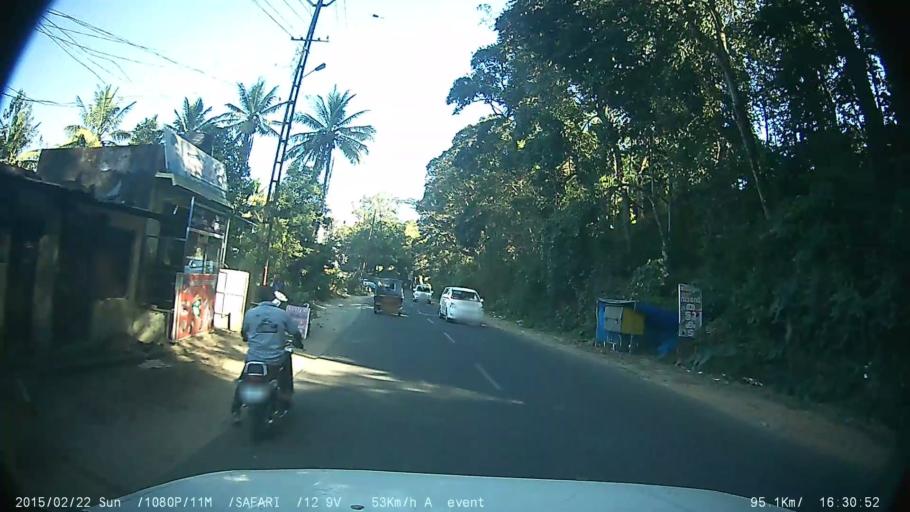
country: IN
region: Tamil Nadu
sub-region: Theni
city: Gudalur
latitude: 9.6090
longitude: 77.1606
